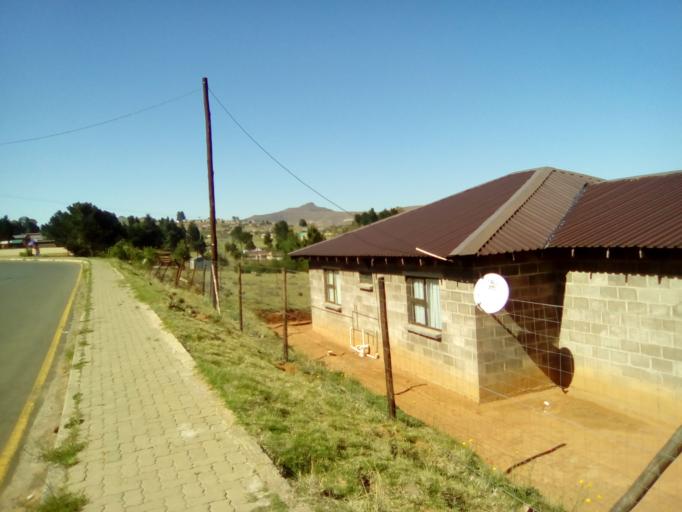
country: LS
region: Qacha's Nek
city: Qacha's Nek
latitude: -30.1080
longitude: 28.6820
